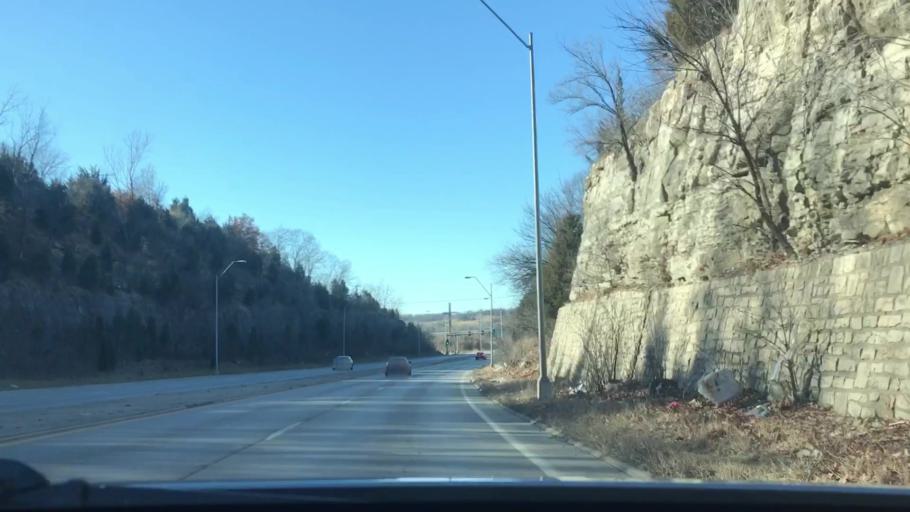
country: US
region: Missouri
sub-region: Jackson County
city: Sugar Creek
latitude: 39.0811
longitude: -94.4843
